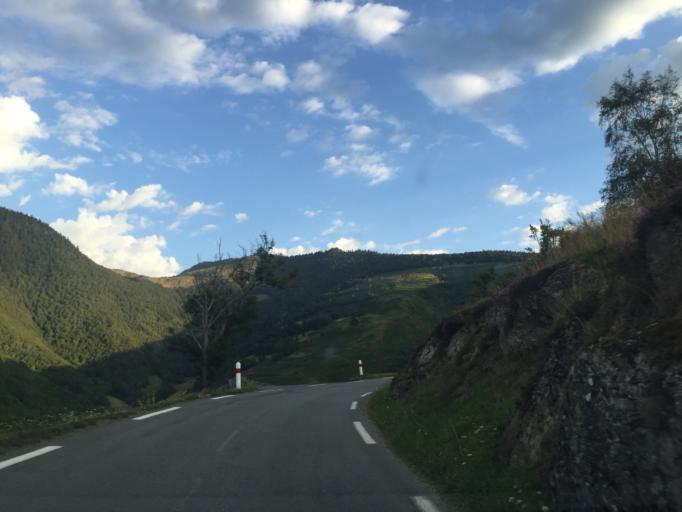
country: FR
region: Midi-Pyrenees
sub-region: Departement des Hautes-Pyrenees
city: Saint-Lary-Soulan
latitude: 42.9268
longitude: 0.3446
